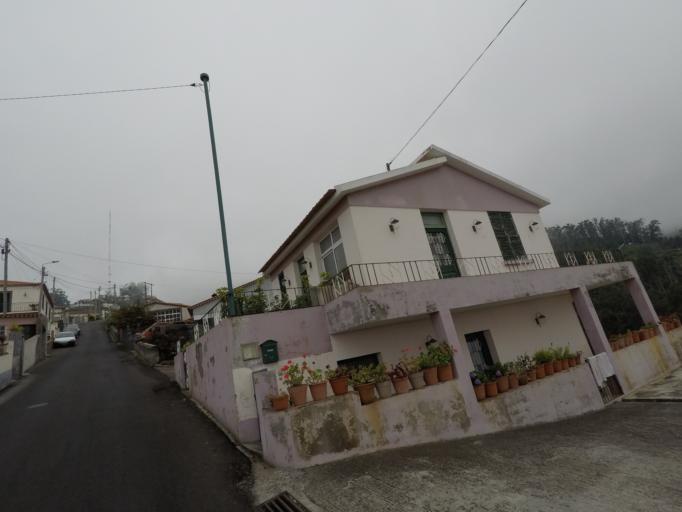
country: PT
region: Madeira
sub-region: Camara de Lobos
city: Curral das Freiras
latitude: 32.6819
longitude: -16.9468
